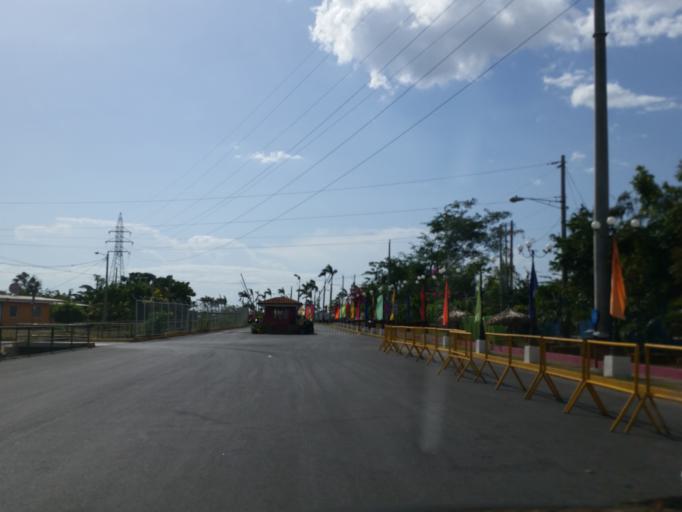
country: NI
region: Managua
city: Managua
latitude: 12.1612
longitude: -86.2754
